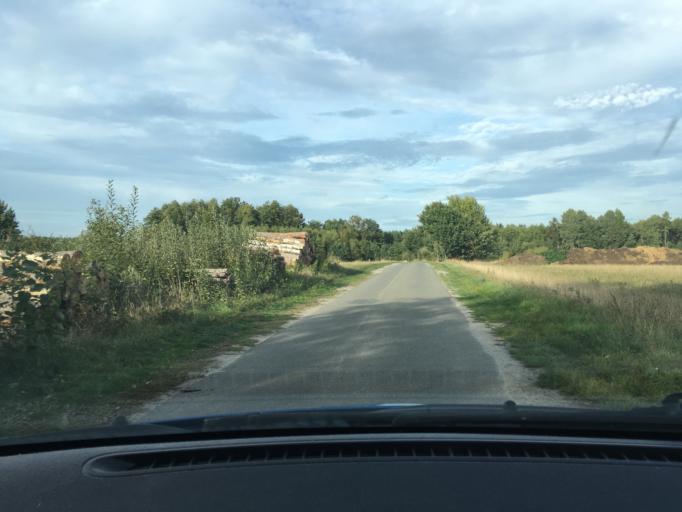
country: DE
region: Lower Saxony
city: Fassberg
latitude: 52.8887
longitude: 10.1221
